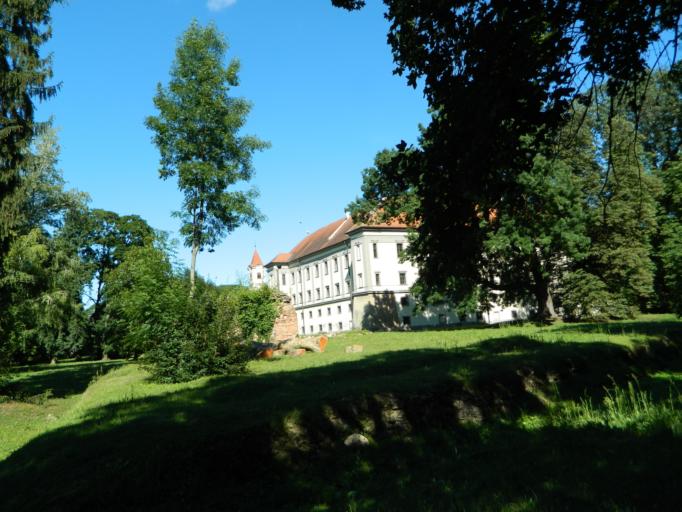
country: HR
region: Medimurska
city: Cakovec
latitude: 46.3891
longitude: 16.4305
